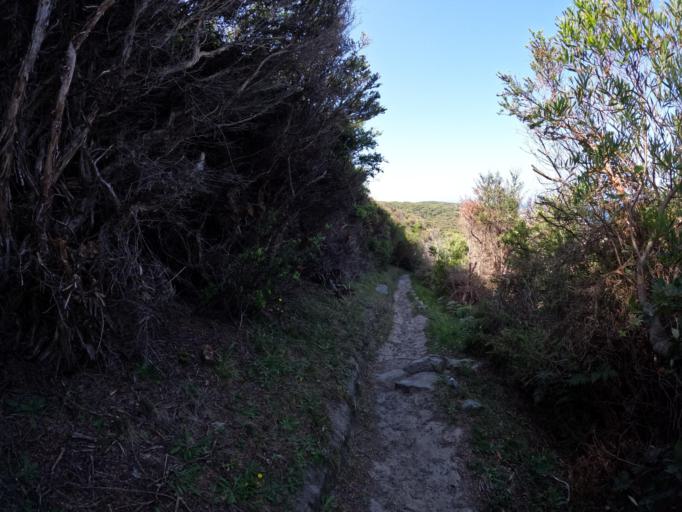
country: AU
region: Victoria
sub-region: Colac-Otway
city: Apollo Bay
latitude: -38.7897
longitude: 143.6476
